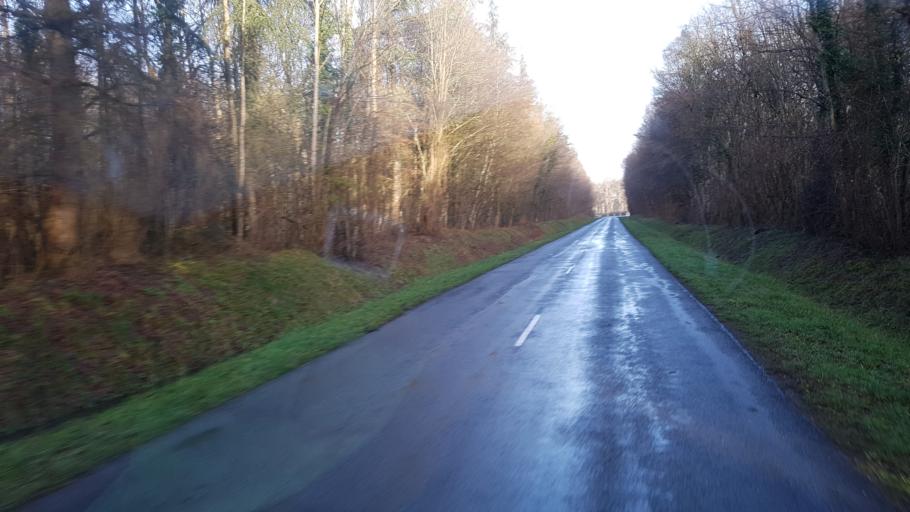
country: FR
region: Centre
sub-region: Departement du Loiret
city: Fay-aux-Loges
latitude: 47.9982
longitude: 2.1952
